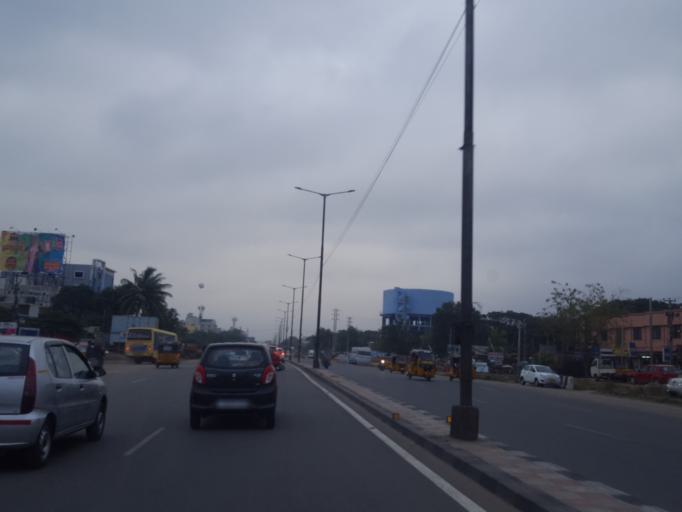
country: IN
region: Telangana
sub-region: Medak
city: Serilingampalle
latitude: 17.5080
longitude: 78.3023
